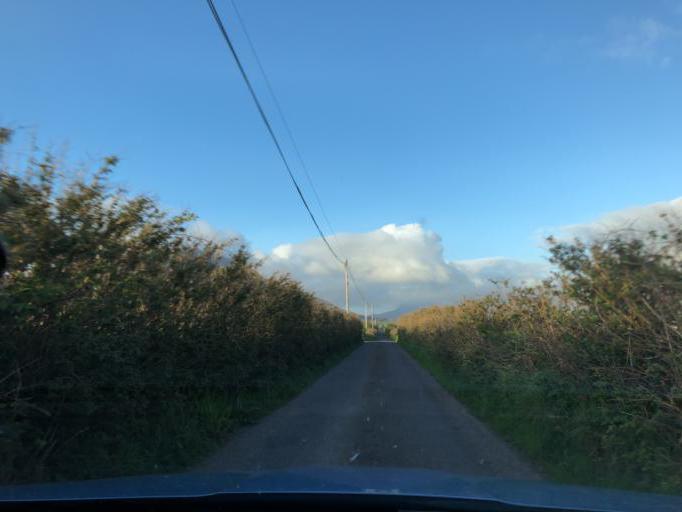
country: IE
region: Munster
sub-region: Ciarrai
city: Cahersiveen
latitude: 51.9607
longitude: -10.2180
